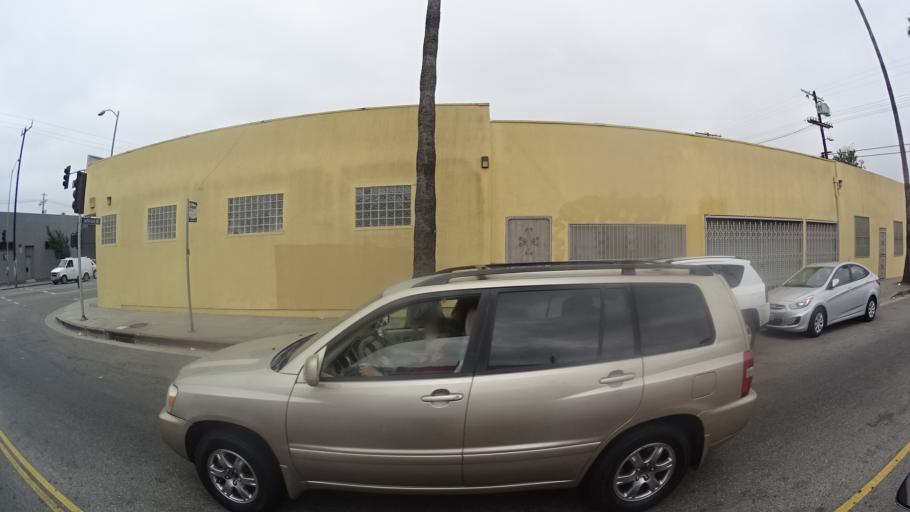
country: US
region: California
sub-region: Los Angeles County
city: View Park-Windsor Hills
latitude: 34.0258
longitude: -118.3405
